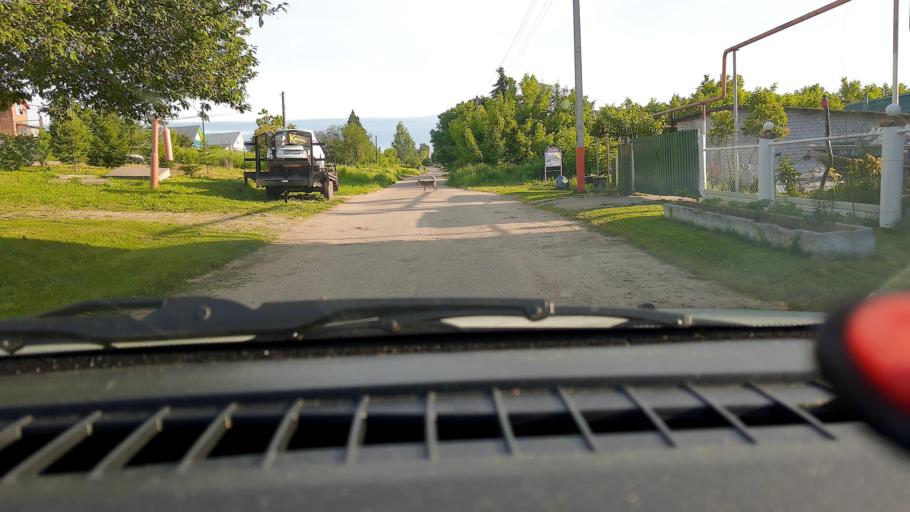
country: RU
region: Nizjnij Novgorod
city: Afonino
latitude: 56.1268
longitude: 44.0276
